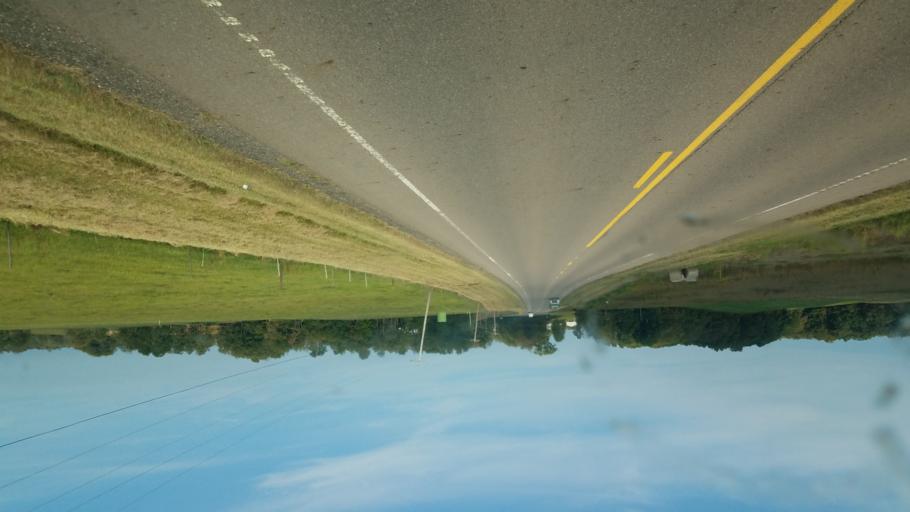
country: US
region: Ohio
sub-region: Licking County
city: Utica
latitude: 40.2621
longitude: -82.4008
